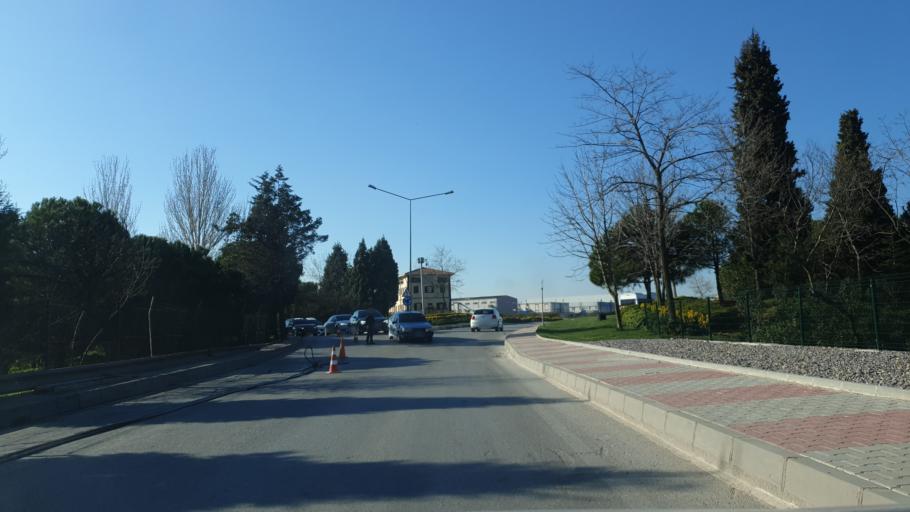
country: TR
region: Istanbul
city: Icmeler
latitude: 40.8798
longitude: 29.3580
